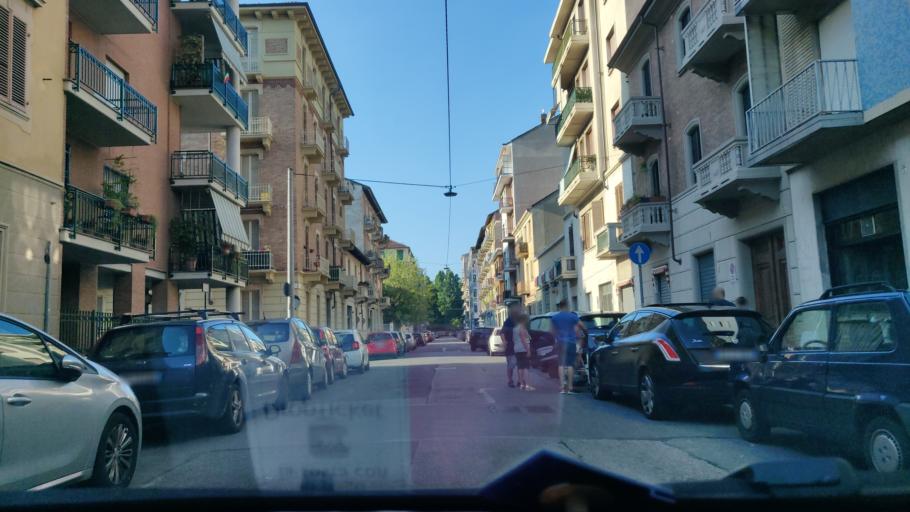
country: IT
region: Piedmont
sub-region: Provincia di Torino
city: Lesna
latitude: 45.0726
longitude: 7.6380
